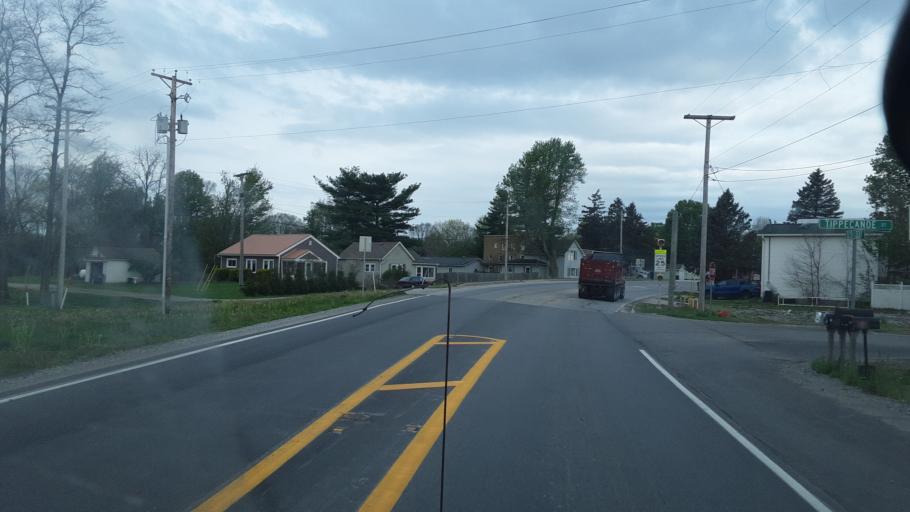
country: US
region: Indiana
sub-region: Noble County
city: Albion
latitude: 41.3332
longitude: -85.4923
